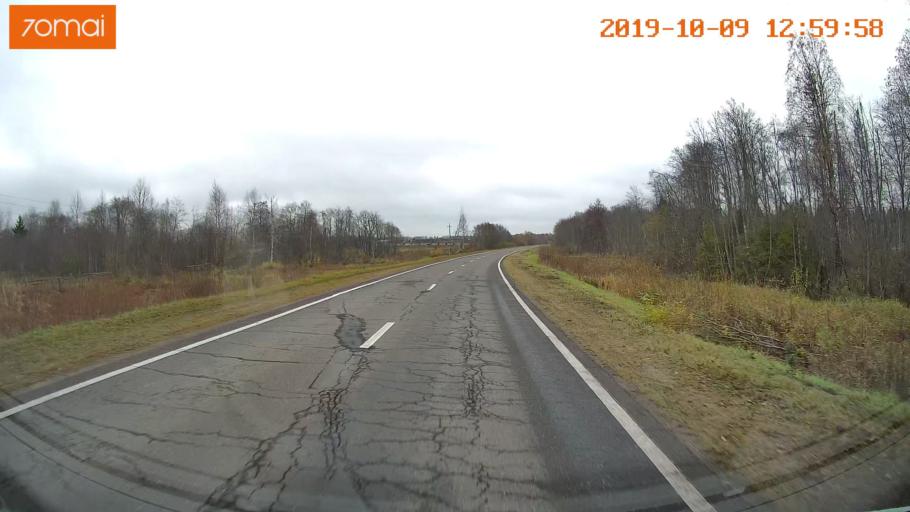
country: RU
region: Jaroslavl
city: Prechistoye
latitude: 58.3810
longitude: 40.4735
